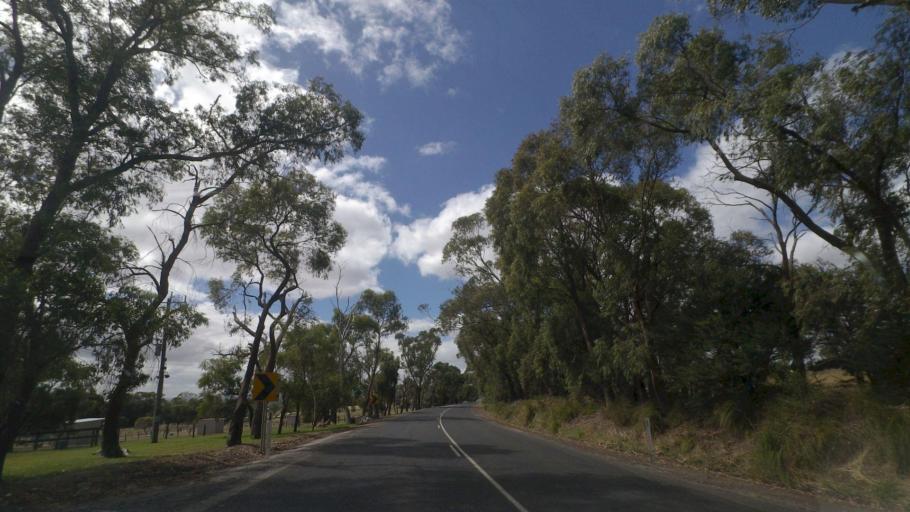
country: AU
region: Victoria
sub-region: Cardinia
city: Koo-Wee-Rup
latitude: -38.3116
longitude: 145.6581
